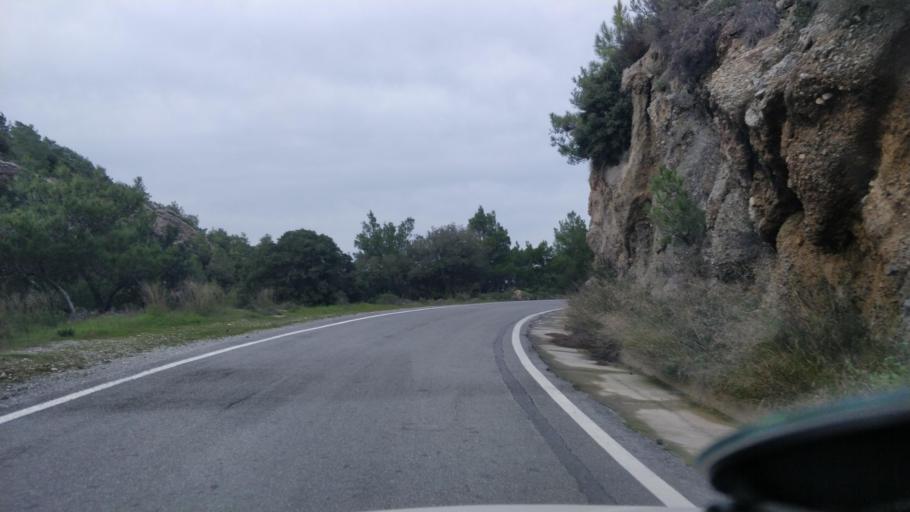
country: GR
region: Crete
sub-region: Nomos Lasithiou
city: Kritsa
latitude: 35.0974
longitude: 25.6981
